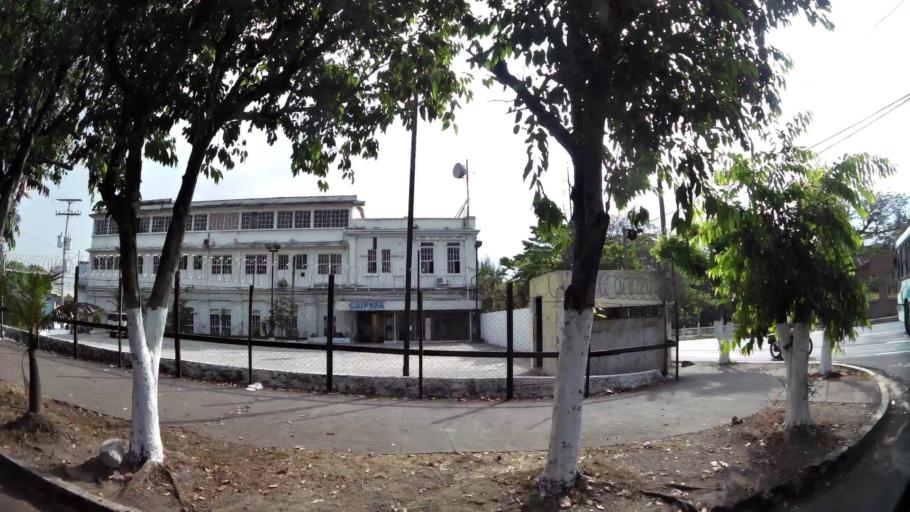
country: SV
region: San Salvador
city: San Salvador
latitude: 13.7000
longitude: -89.2086
